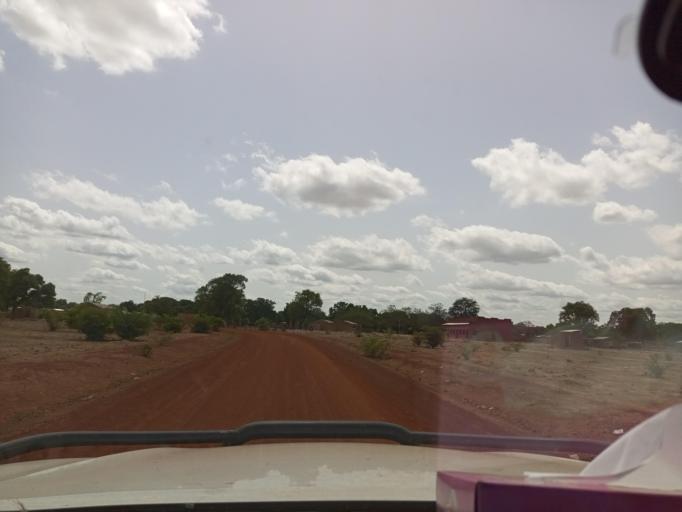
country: ML
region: Sikasso
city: Kolondieba
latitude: 11.5943
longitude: -6.6650
